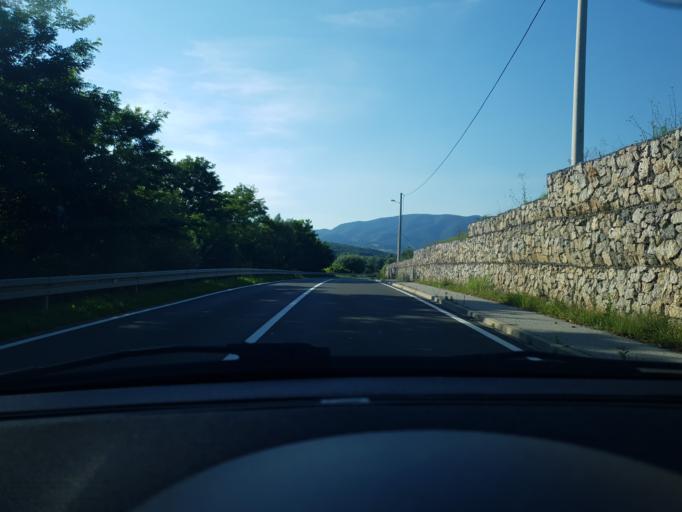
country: HR
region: Krapinsko-Zagorska
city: Mihovljan
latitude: 46.1336
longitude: 15.9382
